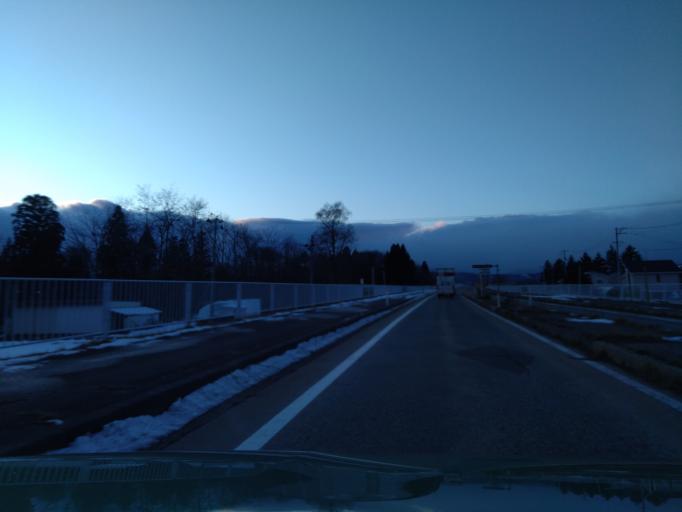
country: JP
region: Iwate
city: Shizukuishi
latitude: 39.6896
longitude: 140.9911
